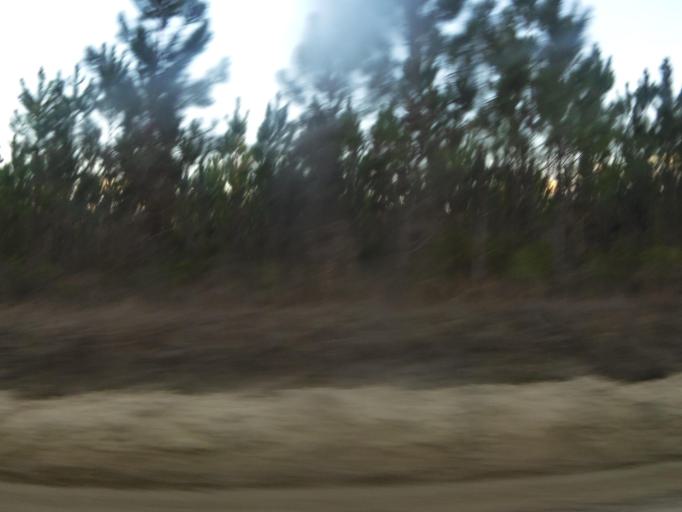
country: US
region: Florida
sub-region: Clay County
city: Green Cove Springs
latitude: 29.8443
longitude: -81.7970
